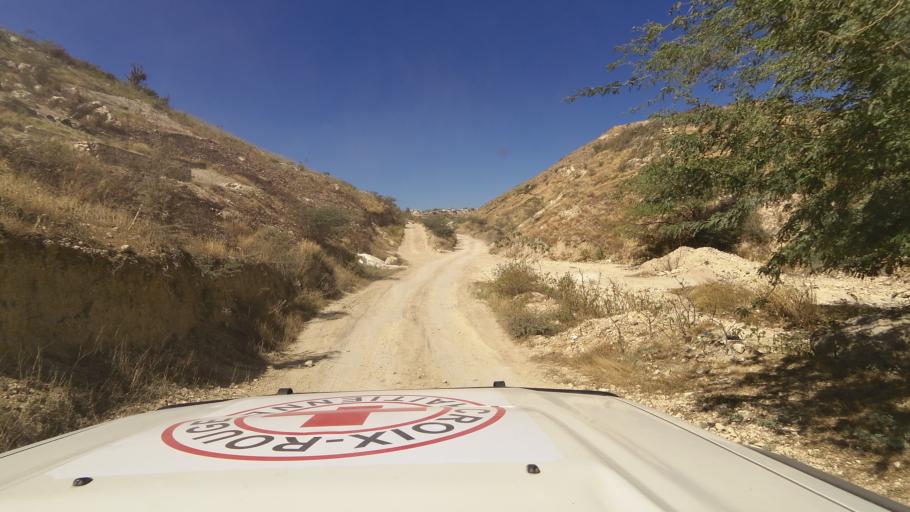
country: HT
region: Ouest
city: Croix des Bouquets
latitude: 18.6661
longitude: -72.2737
